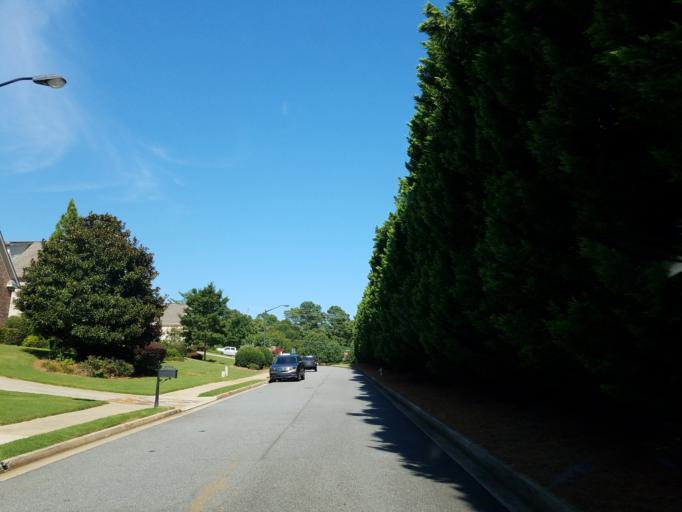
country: US
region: Georgia
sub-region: Cobb County
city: Marietta
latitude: 33.9737
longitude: -84.4633
